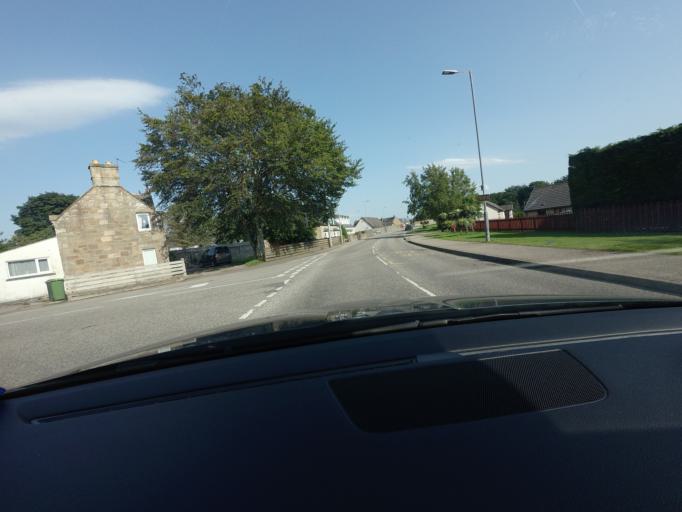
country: GB
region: Scotland
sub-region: Highland
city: Alness
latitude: 57.6950
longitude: -4.2468
